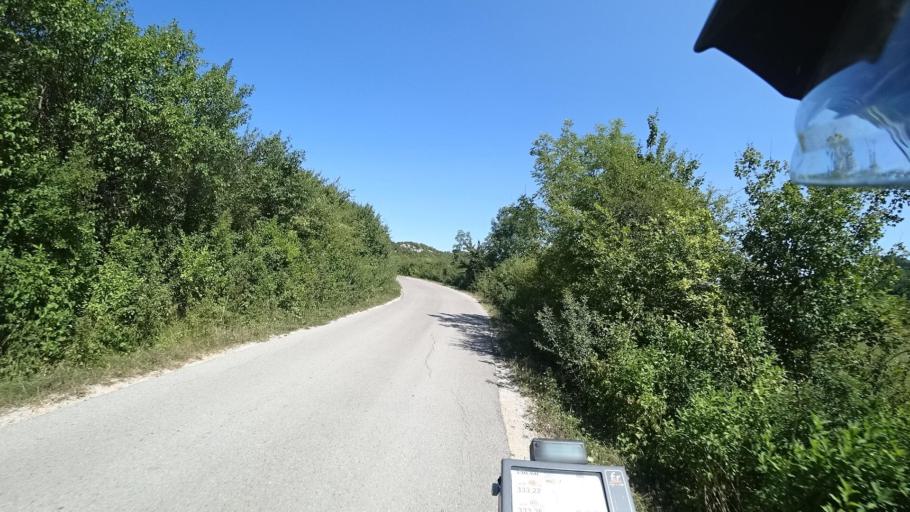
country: HR
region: Licko-Senjska
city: Popovaca
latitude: 44.7114
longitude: 15.2553
